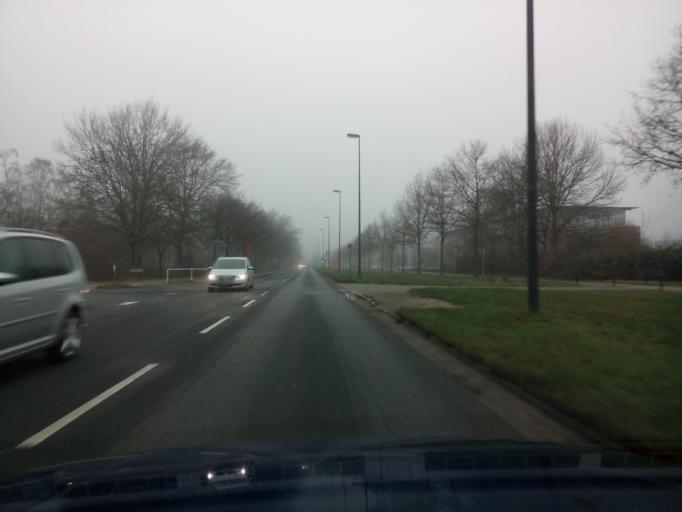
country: DE
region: Bremen
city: Bremen
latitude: 53.1114
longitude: 8.8525
